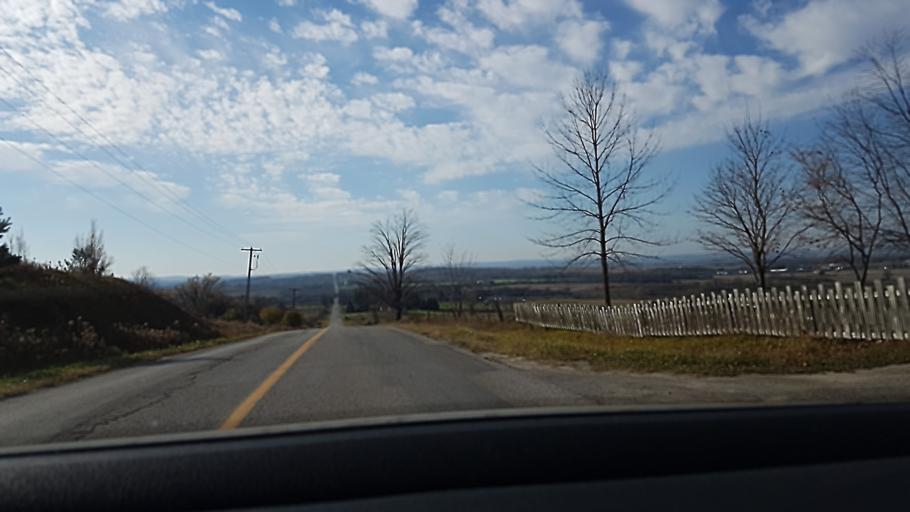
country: CA
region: Ontario
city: Bradford West Gwillimbury
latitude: 44.0653
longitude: -79.7863
